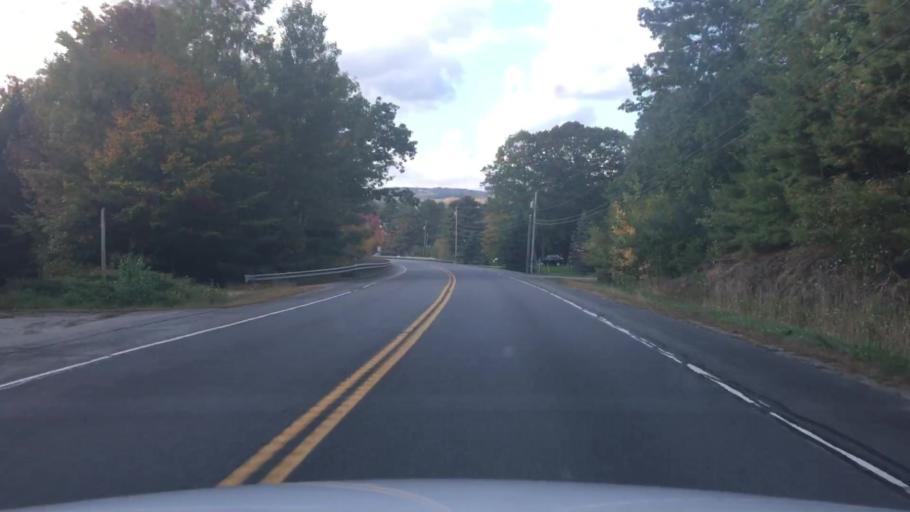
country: US
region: Maine
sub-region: Knox County
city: Union
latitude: 44.2152
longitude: -69.2681
